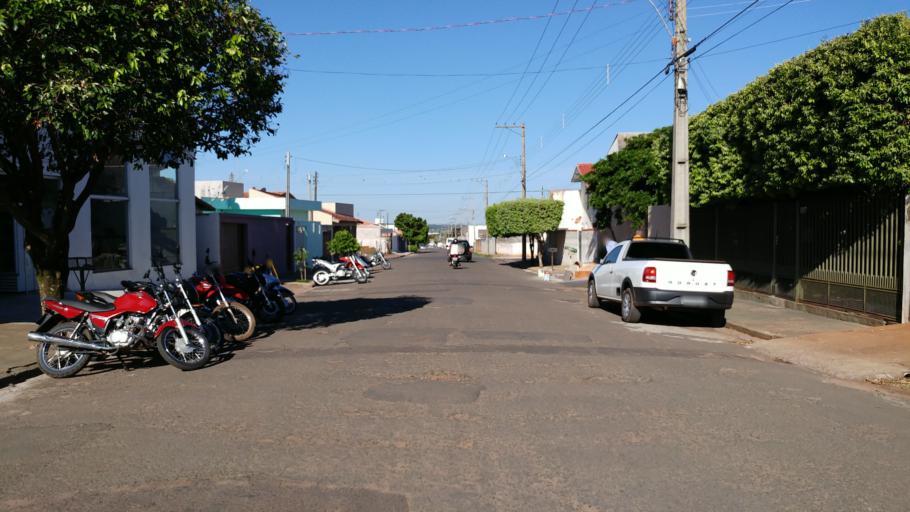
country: BR
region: Sao Paulo
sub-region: Paraguacu Paulista
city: Paraguacu Paulista
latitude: -22.4241
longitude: -50.5786
